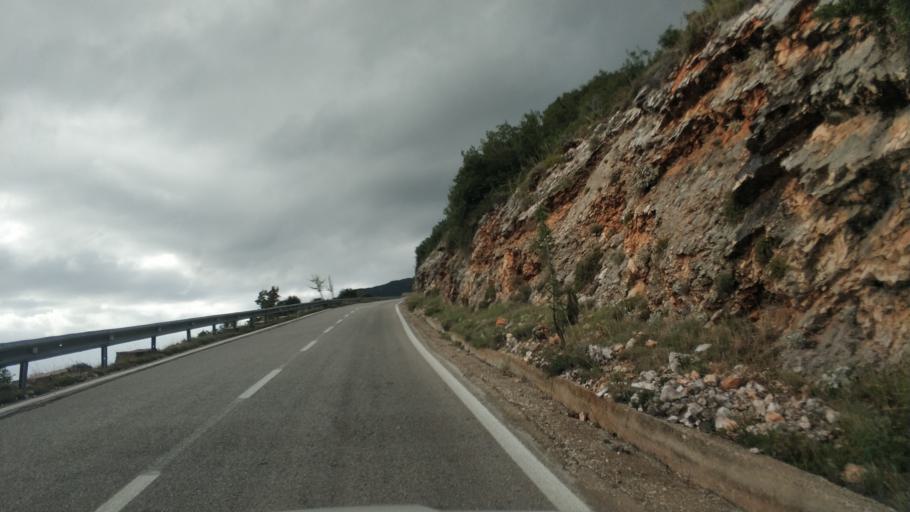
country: AL
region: Vlore
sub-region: Rrethi i Vlores
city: Vranisht
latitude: 40.1781
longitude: 19.6003
